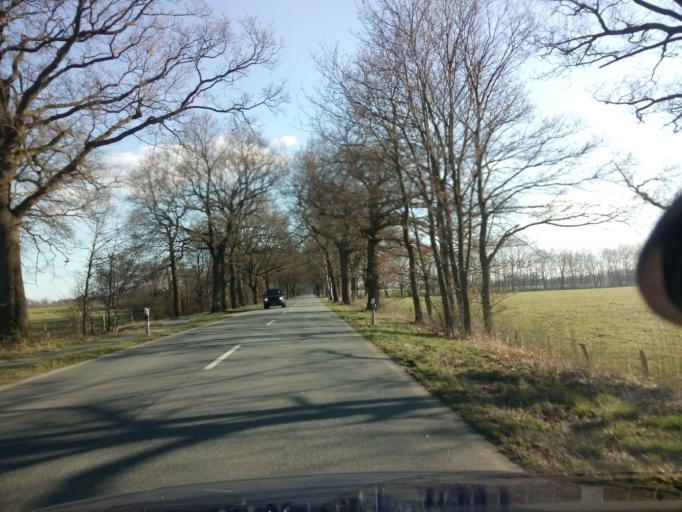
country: DE
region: Lower Saxony
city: Osterholz-Scharmbeck
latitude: 53.2599
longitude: 8.7690
